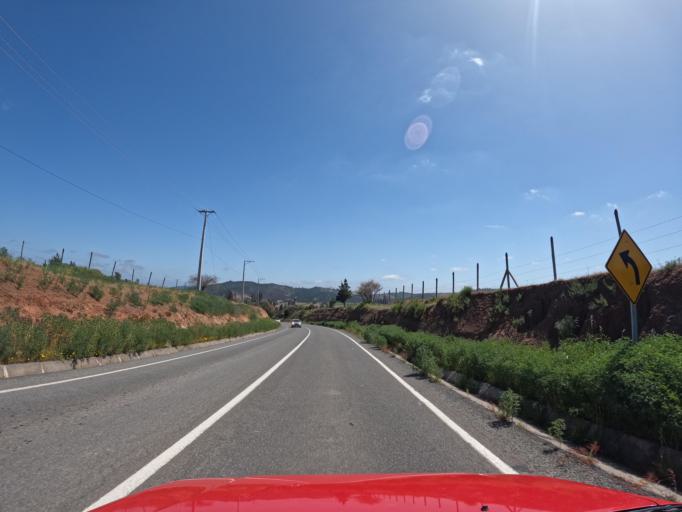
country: CL
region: O'Higgins
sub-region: Provincia de Colchagua
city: Santa Cruz
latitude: -34.6540
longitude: -71.8622
